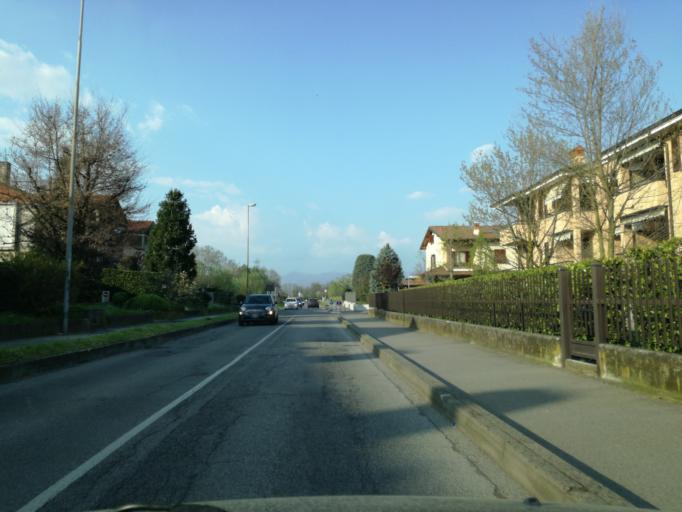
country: IT
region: Lombardy
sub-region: Provincia di Monza e Brianza
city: Carnate
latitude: 45.6535
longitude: 9.3830
